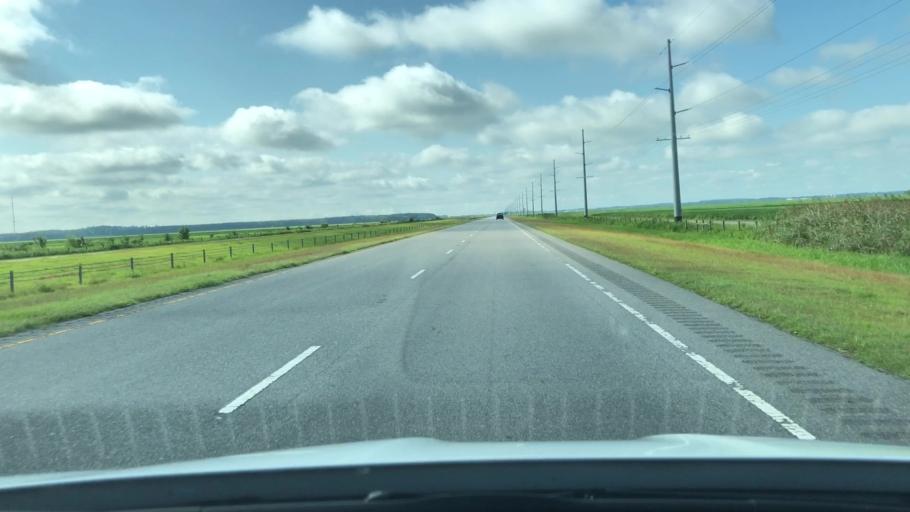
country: US
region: North Carolina
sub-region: Pasquotank County
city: Elizabeth City
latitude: 36.3269
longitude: -76.3108
